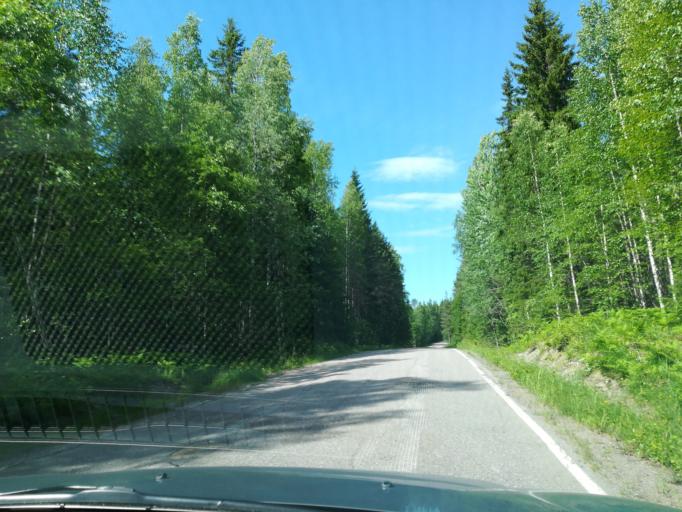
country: FI
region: South Karelia
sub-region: Imatra
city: Ruokolahti
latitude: 61.4810
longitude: 28.8736
